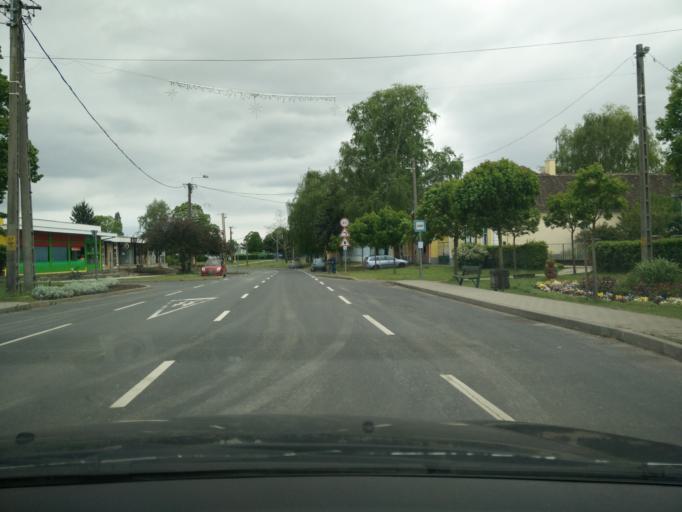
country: HU
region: Zala
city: Turje
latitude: 46.9832
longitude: 17.1051
